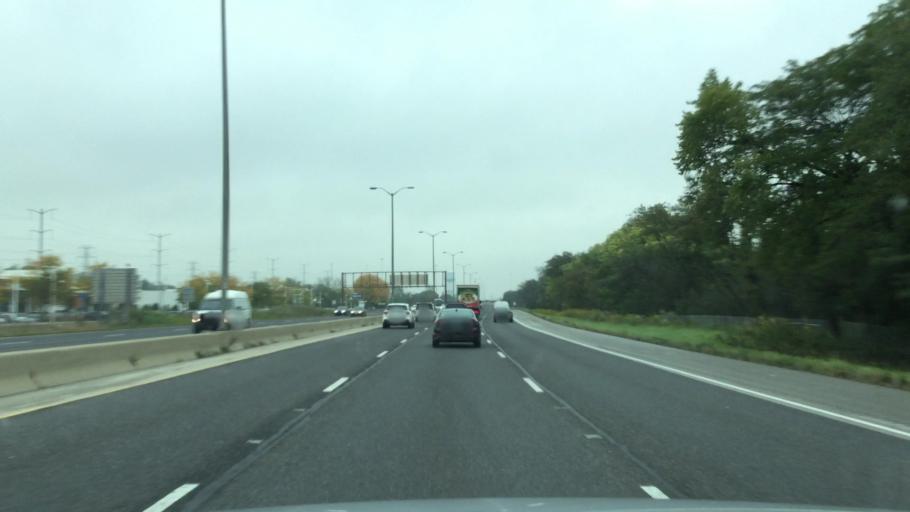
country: US
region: Illinois
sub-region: Cook County
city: Northfield
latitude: 42.1092
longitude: -87.7731
